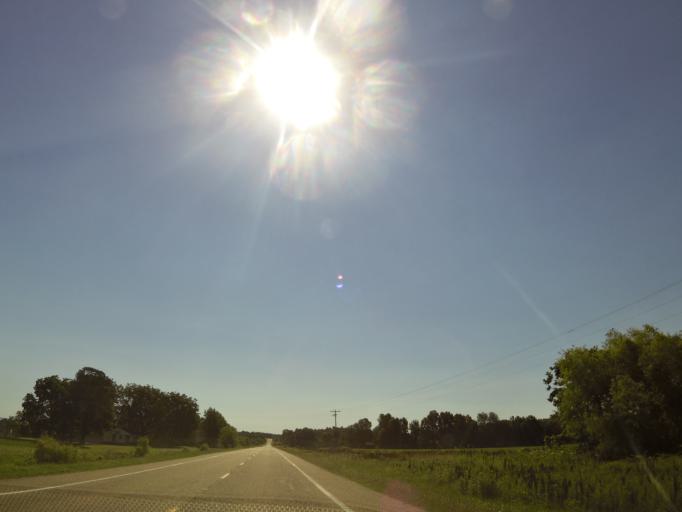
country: US
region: Arkansas
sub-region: Clay County
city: Piggott
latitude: 36.4338
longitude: -90.3440
